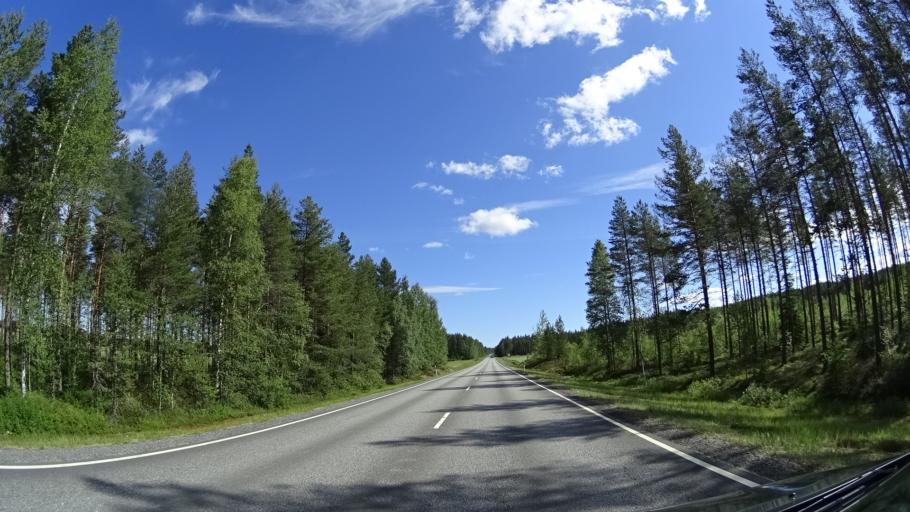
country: FI
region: Pirkanmaa
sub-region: Luoteis-Pirkanmaa
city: Kihnioe
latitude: 62.2090
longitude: 23.2386
